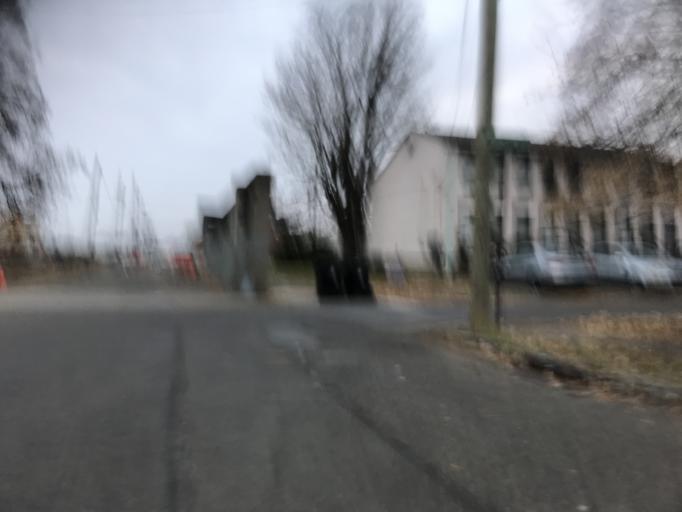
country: US
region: Indiana
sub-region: Clark County
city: Jeffersonville
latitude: 38.2563
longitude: -85.7325
